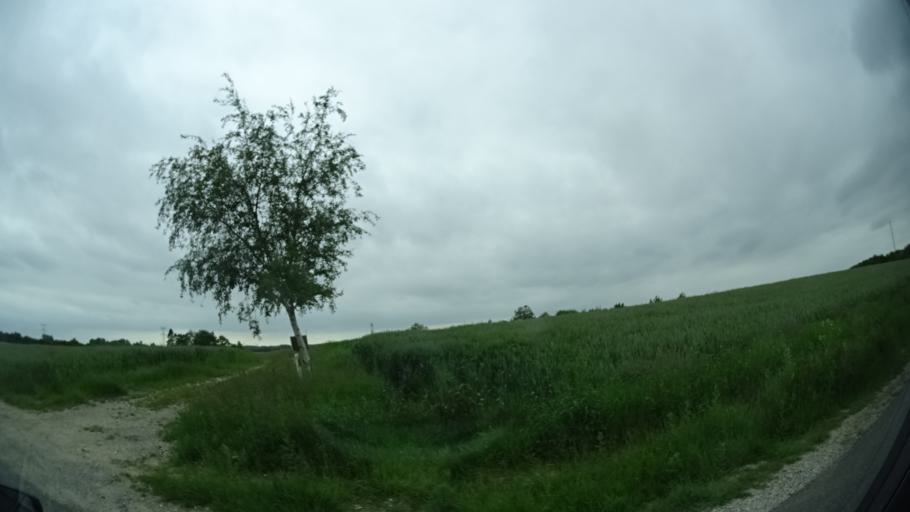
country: DK
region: Central Jutland
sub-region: Arhus Kommune
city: Kolt
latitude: 56.1055
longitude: 10.0576
